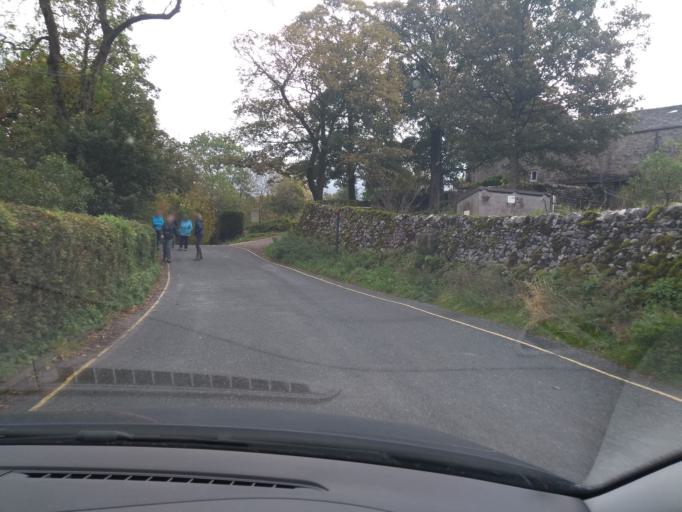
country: GB
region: England
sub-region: North Yorkshire
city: Gargrave
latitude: 54.0647
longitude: -2.1557
